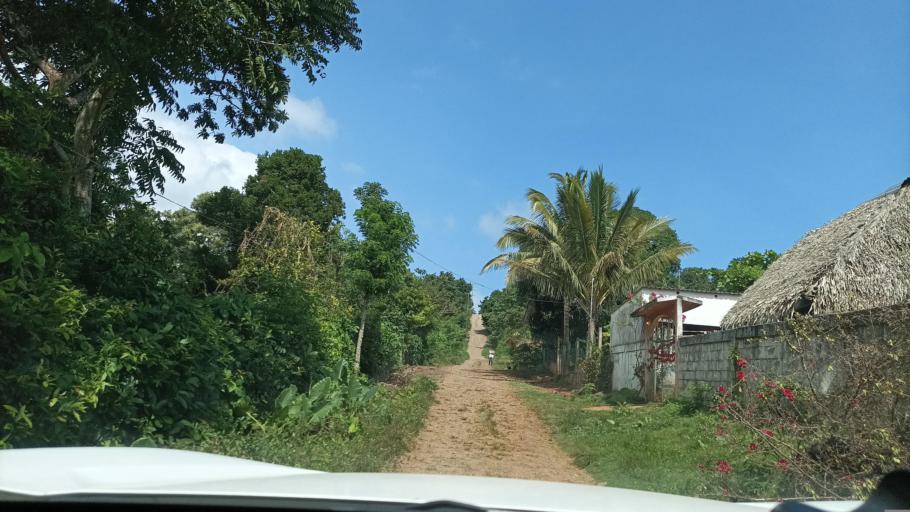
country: MX
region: Veracruz
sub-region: Pajapan
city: Pajapan
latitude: 18.2663
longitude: -94.6840
